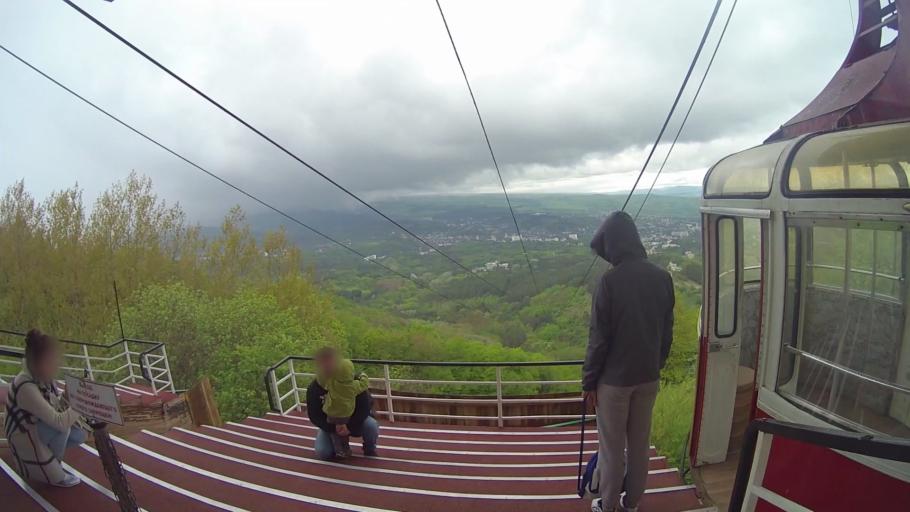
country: RU
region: Stavropol'skiy
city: Kislovodsk
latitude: 43.8985
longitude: 42.7586
